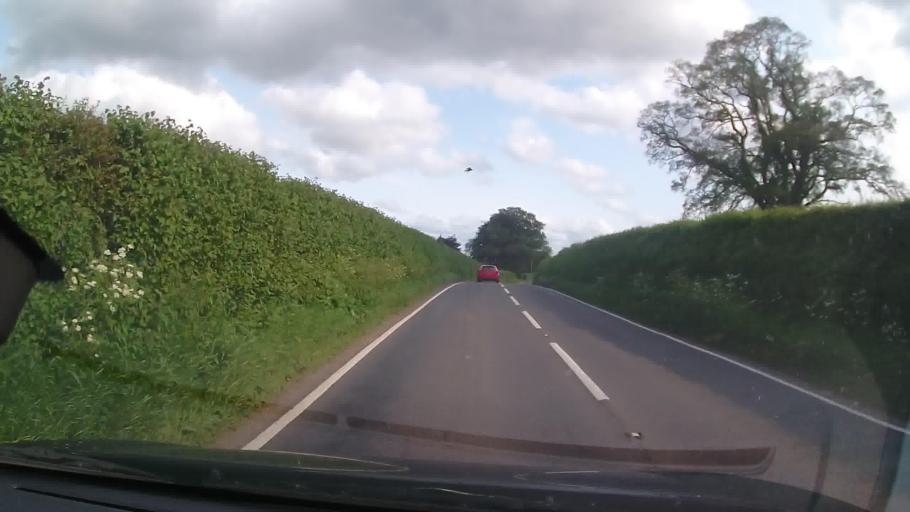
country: GB
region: England
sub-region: Shropshire
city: Clive
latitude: 52.7652
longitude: -2.7474
